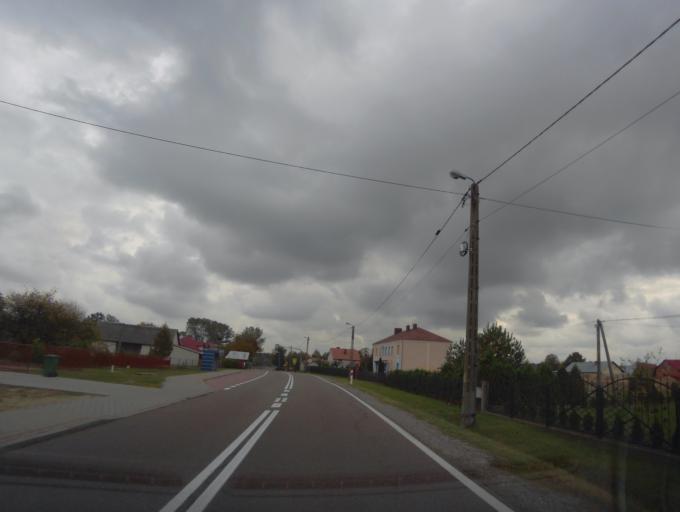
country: PL
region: Subcarpathian Voivodeship
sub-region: Powiat nizanski
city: Krzeszow
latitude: 50.3691
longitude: 22.3163
